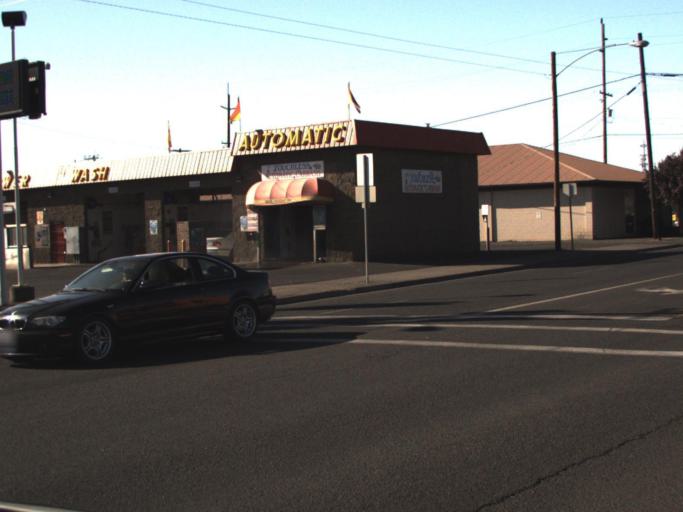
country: US
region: Washington
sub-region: Walla Walla County
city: Walla Walla
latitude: 46.0632
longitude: -118.3486
